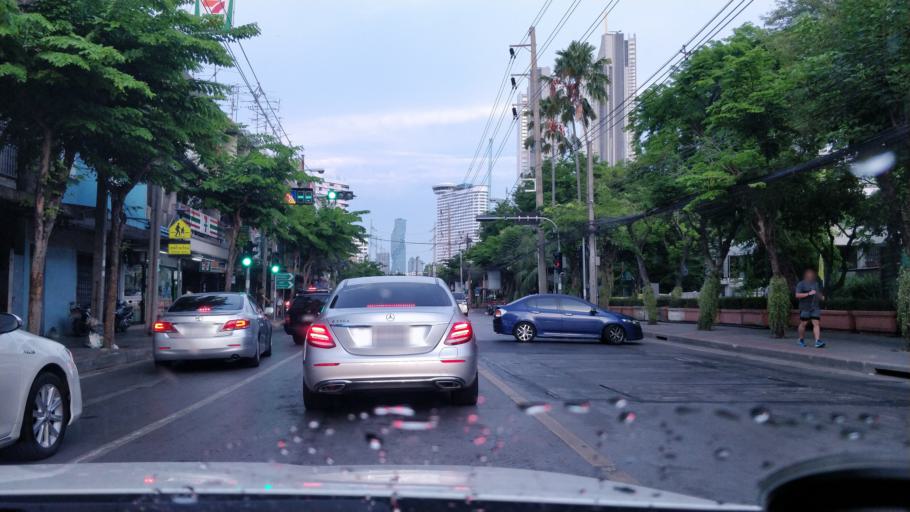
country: TH
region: Bangkok
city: Khlong San
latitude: 13.7315
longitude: 100.5045
